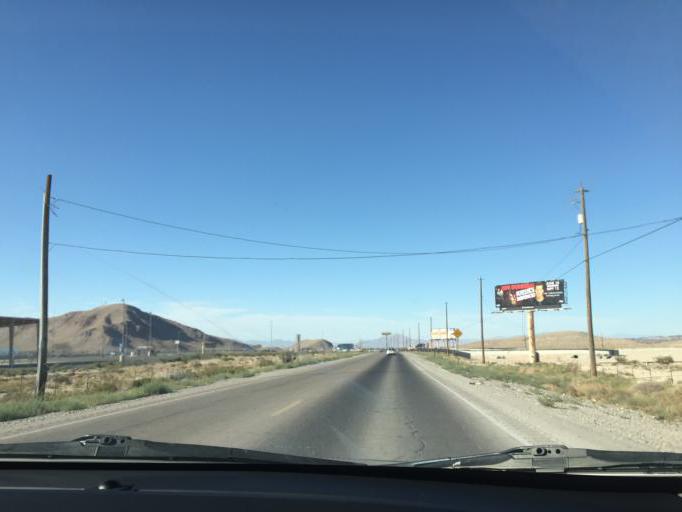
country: US
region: Nevada
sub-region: Clark County
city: Enterprise
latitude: 35.9260
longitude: -115.1948
